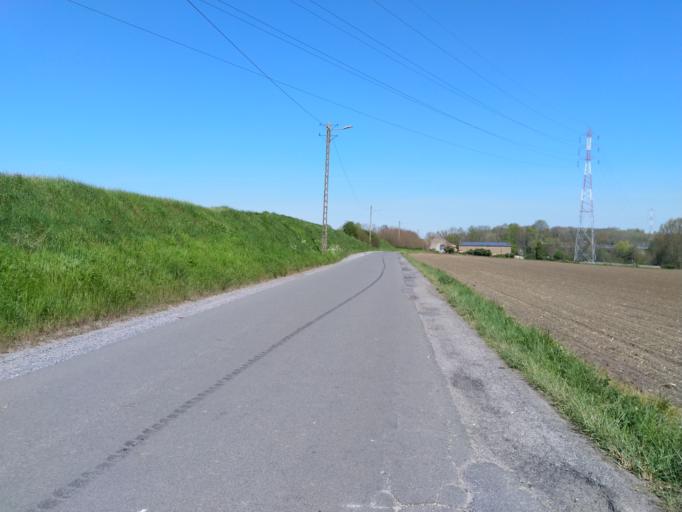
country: BE
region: Wallonia
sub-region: Province du Hainaut
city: Mons
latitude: 50.4841
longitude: 4.0135
